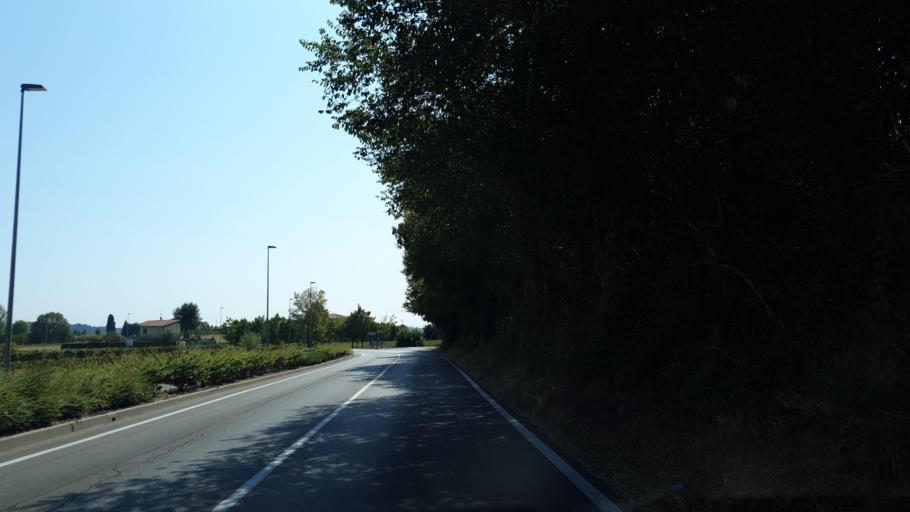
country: IT
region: Lombardy
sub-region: Provincia di Brescia
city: Calvagese della Riviera
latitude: 45.5295
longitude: 10.4475
